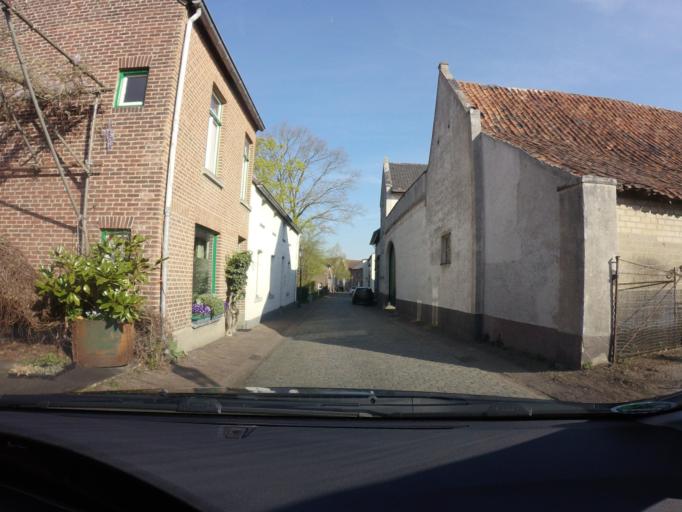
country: NL
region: Limburg
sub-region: Gemeente Stein
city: Elsloo
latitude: 50.9461
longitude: 5.7617
